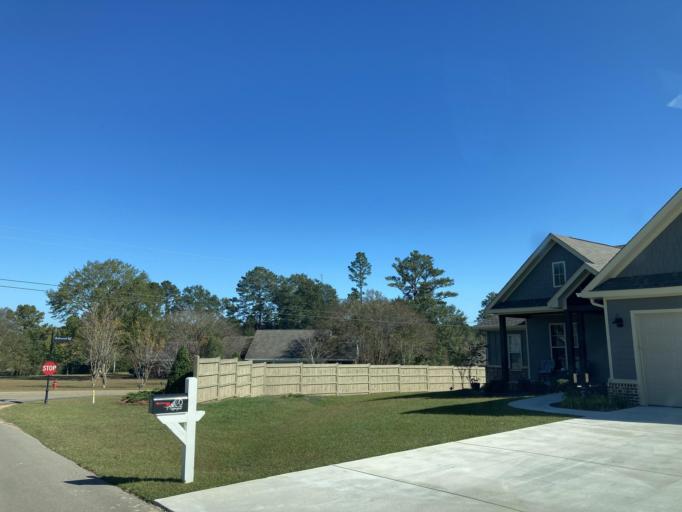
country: US
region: Mississippi
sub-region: Lamar County
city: West Hattiesburg
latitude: 31.2991
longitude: -89.4166
